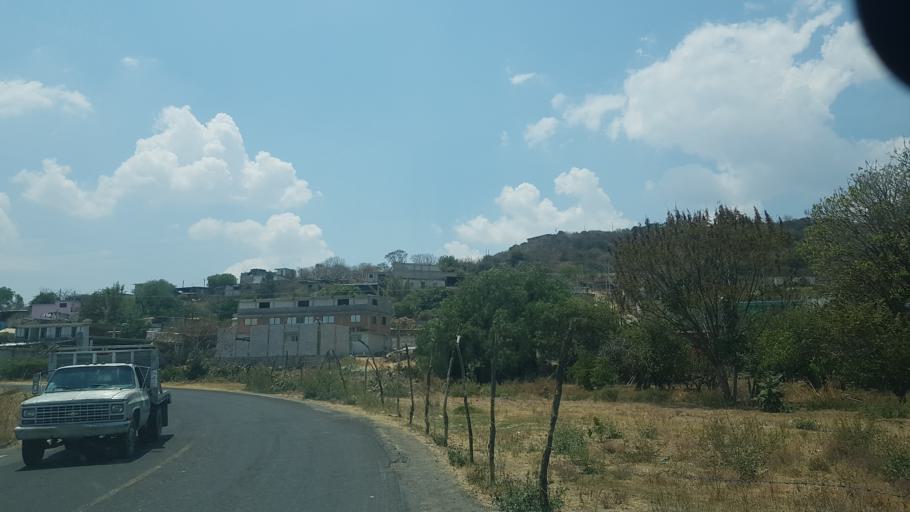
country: MX
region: Puebla
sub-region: Atzitzihuacan
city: Santiago Atzitzihuacan
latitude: 18.8359
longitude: -98.5957
